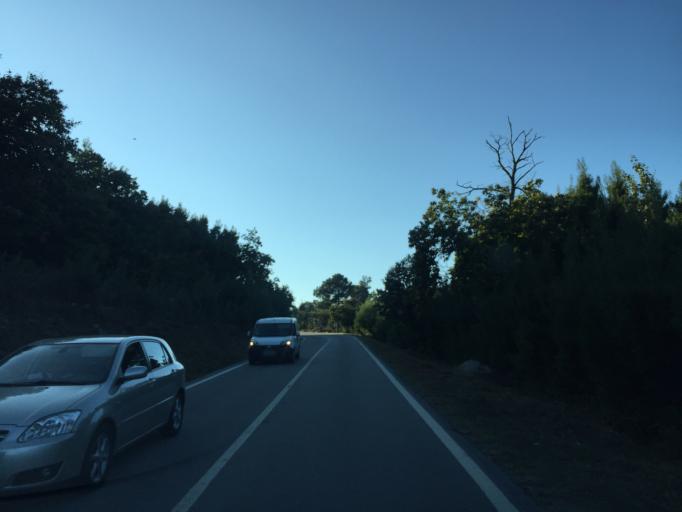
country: PT
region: Portalegre
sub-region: Castelo de Vide
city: Castelo de Vide
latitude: 39.4016
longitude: -7.4349
